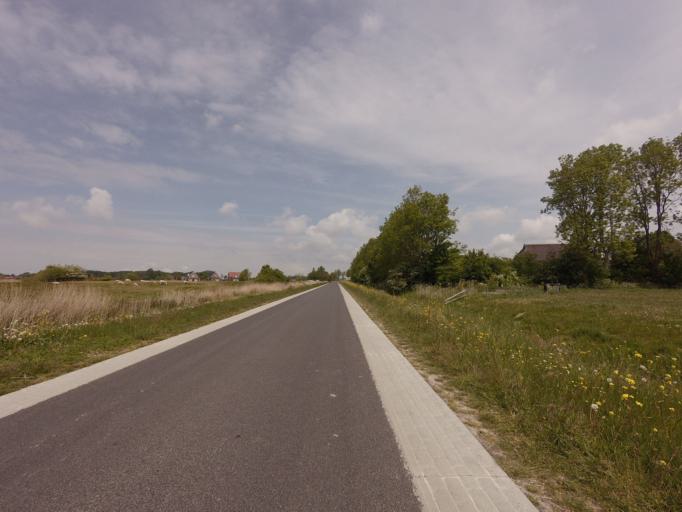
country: NL
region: Friesland
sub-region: Sudwest Fryslan
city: Bolsward
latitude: 53.0976
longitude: 5.4786
